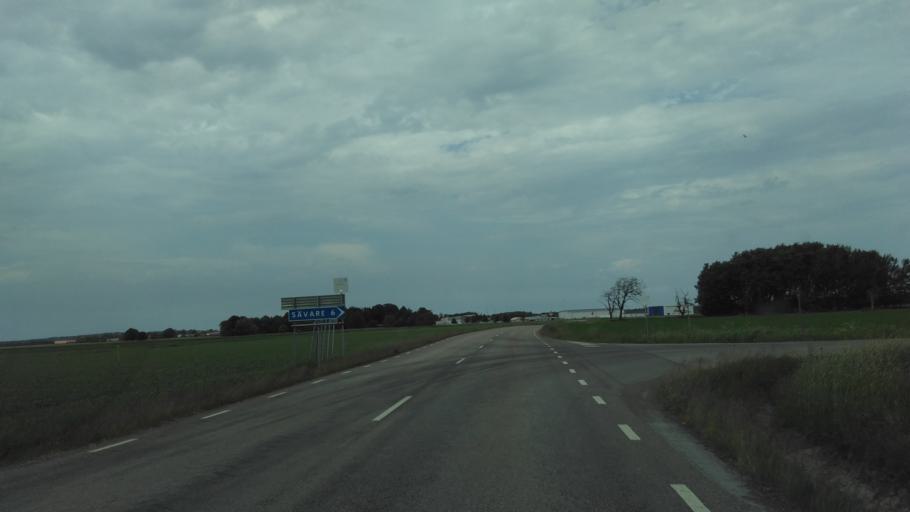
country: SE
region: Vaestra Goetaland
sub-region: Lidkopings Kommun
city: Lidkoping
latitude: 58.4554
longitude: 13.1570
